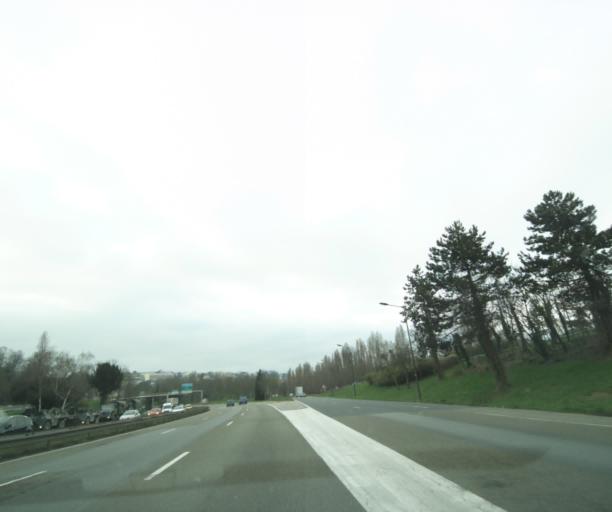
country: FR
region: Ile-de-France
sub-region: Departement des Yvelines
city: Le Port-Marly
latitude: 48.8848
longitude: 2.1061
